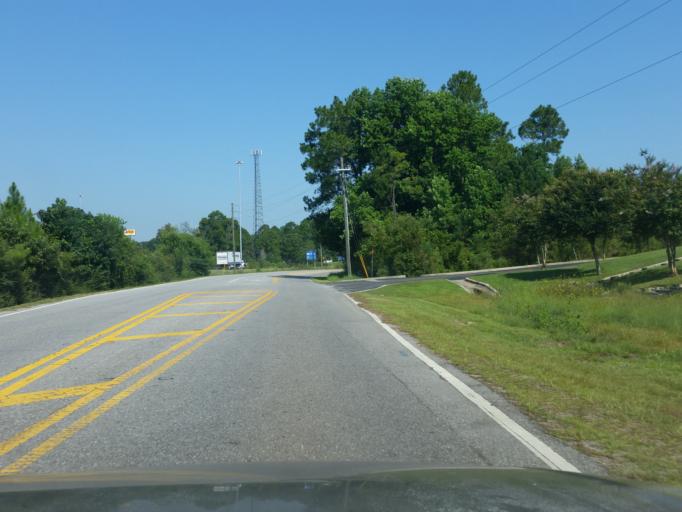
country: US
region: Florida
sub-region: Escambia County
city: Ensley
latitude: 30.5202
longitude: -87.3100
